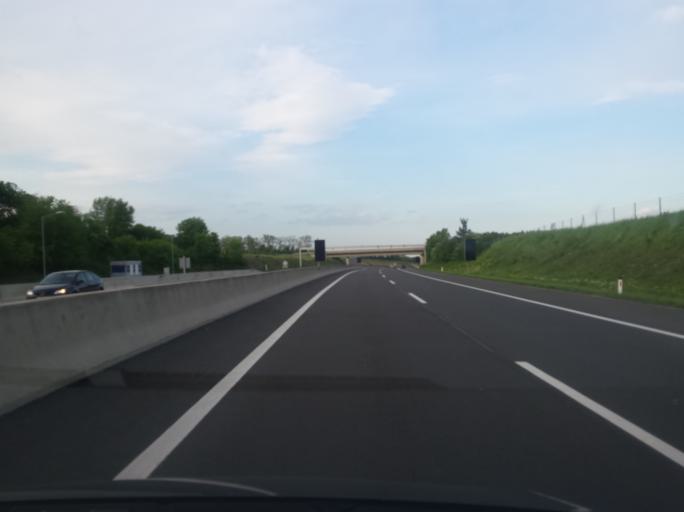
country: AT
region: Burgenland
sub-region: Politischer Bezirk Mattersburg
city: Hirm
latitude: 47.7935
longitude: 16.4484
